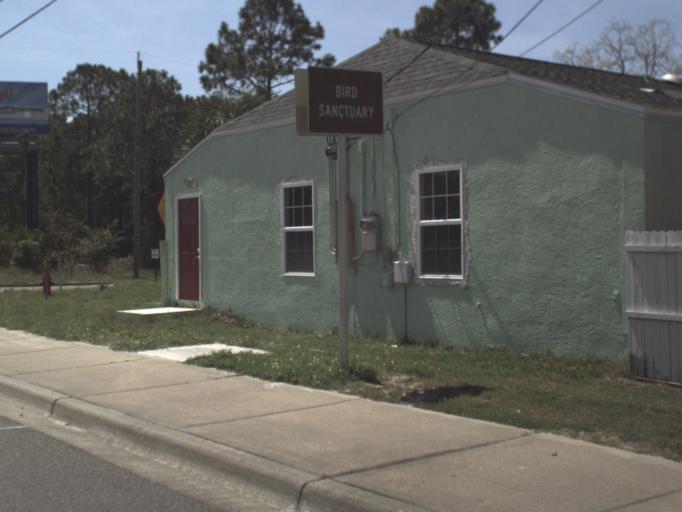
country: US
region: Florida
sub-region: Bay County
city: Laguna Beach
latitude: 30.2341
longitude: -85.8862
